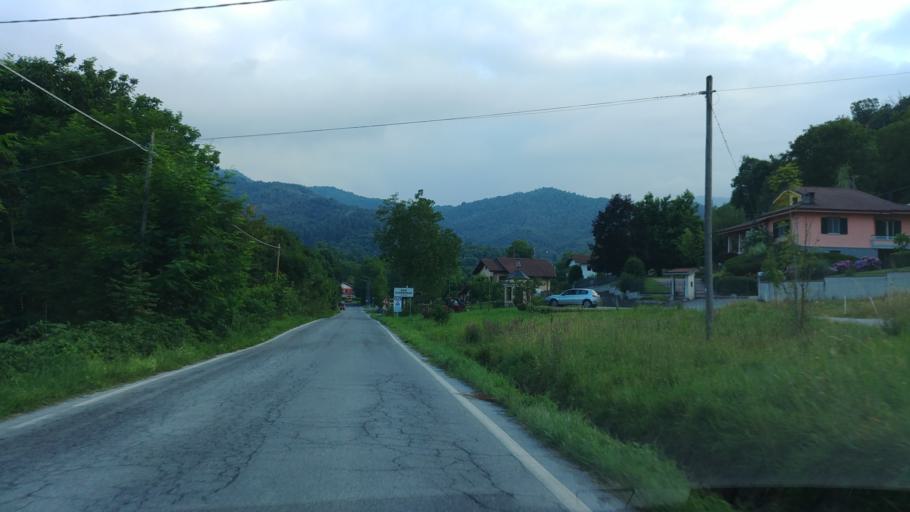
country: IT
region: Piedmont
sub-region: Provincia di Cuneo
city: Peveragno
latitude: 44.3228
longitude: 7.6000
